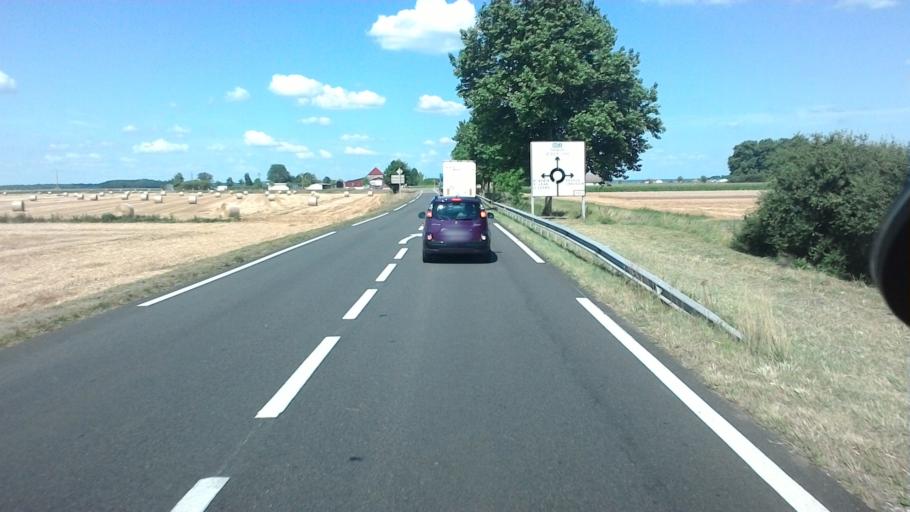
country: FR
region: Franche-Comte
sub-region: Departement du Jura
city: Saint-Aubin
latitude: 47.0013
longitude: 5.3519
